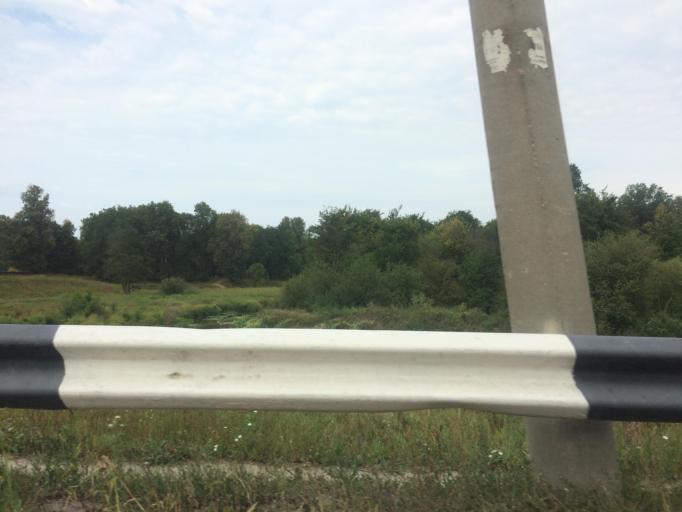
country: RU
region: Mariy-El
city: Yoshkar-Ola
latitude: 56.5481
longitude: 47.9827
